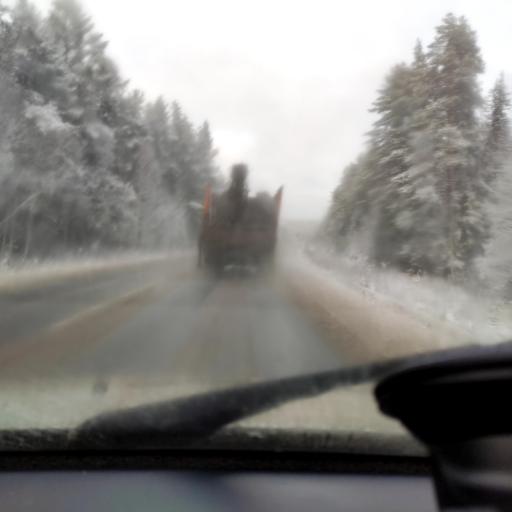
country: RU
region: Perm
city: Nytva
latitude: 57.9731
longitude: 55.3647
